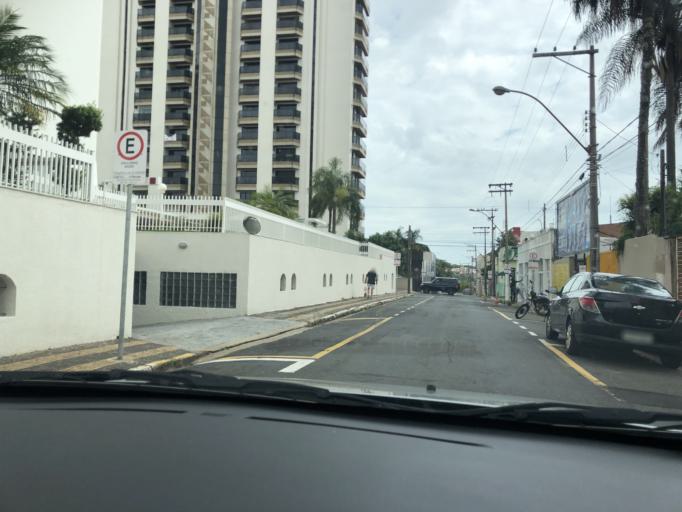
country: BR
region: Sao Paulo
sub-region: Americana
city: Americana
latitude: -22.7395
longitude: -47.3339
